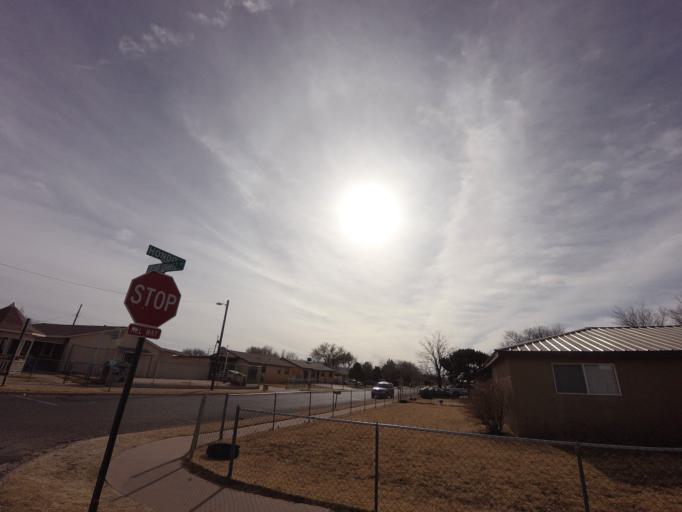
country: US
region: New Mexico
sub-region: Curry County
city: Clovis
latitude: 34.4099
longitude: -103.2376
